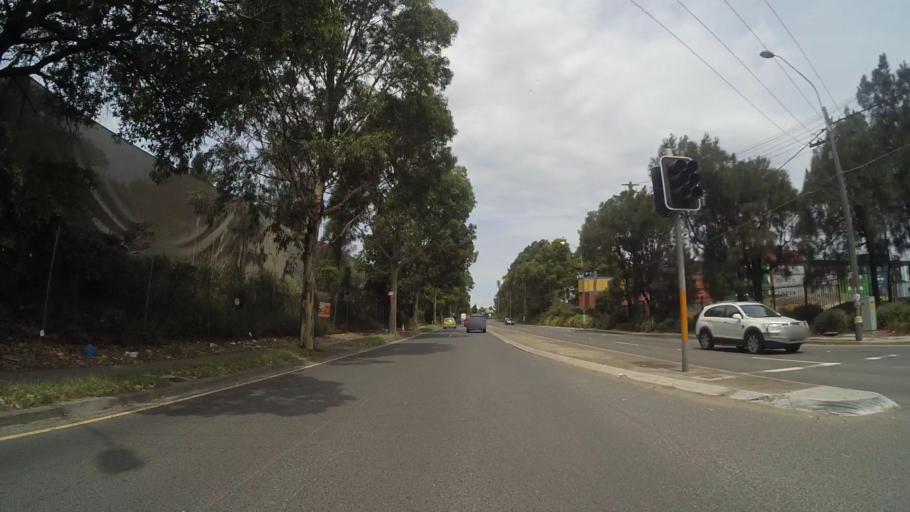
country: AU
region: New South Wales
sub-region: Marrickville
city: Newtown
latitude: -33.9172
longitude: 151.1762
